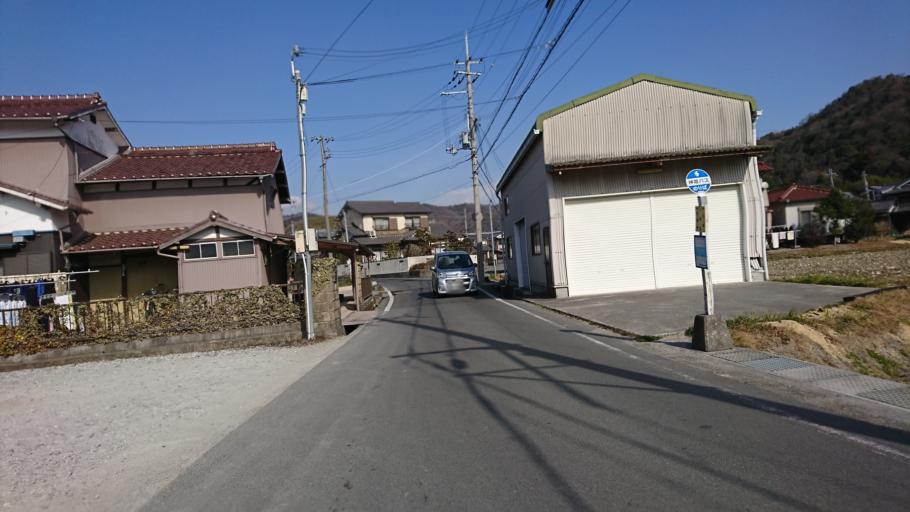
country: JP
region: Hyogo
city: Kakogawacho-honmachi
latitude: 34.8154
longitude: 134.8542
